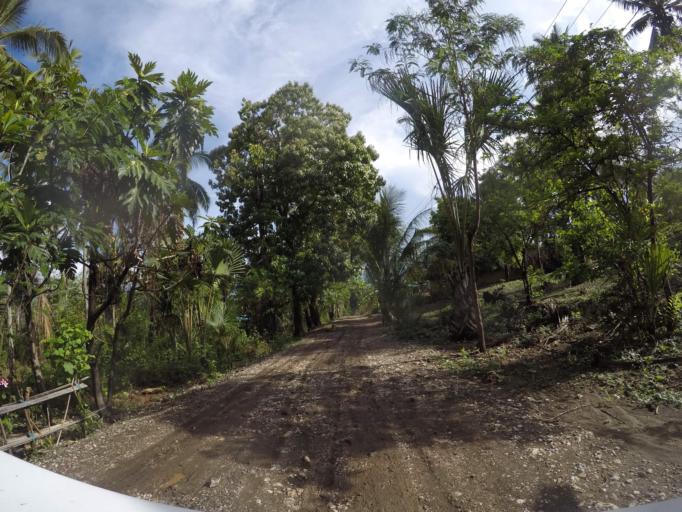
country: TL
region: Baucau
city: Baucau
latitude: -8.5013
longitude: 126.4617
